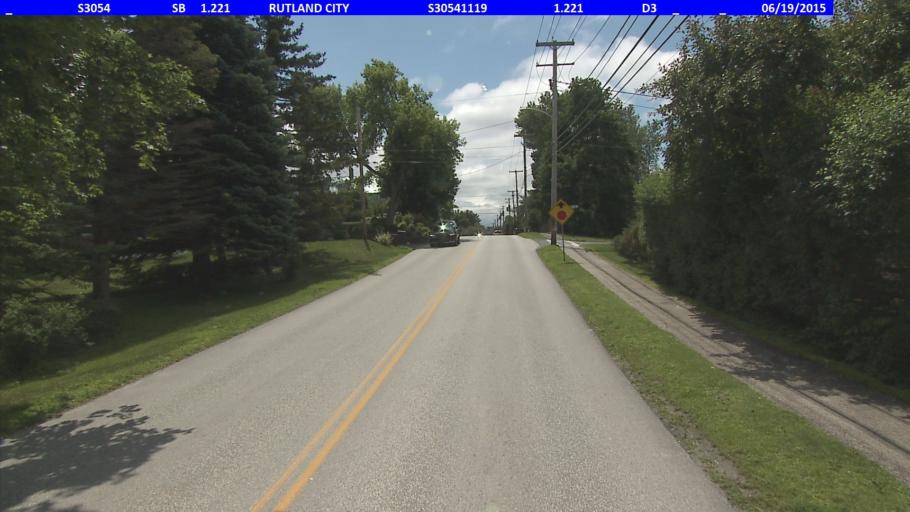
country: US
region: Vermont
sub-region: Rutland County
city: Rutland
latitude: 43.6089
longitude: -72.9565
